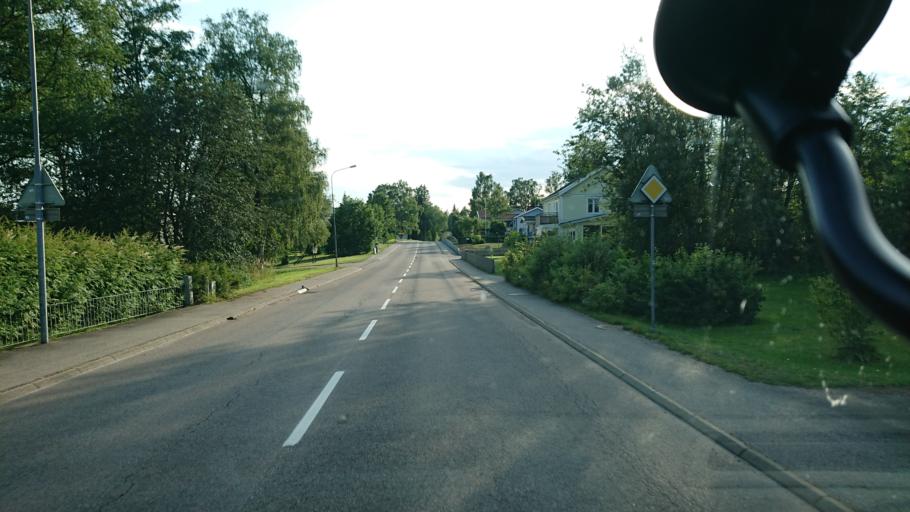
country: SE
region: Kronoberg
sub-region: Vaxjo Kommun
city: Rottne
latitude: 57.0344
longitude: 14.9379
